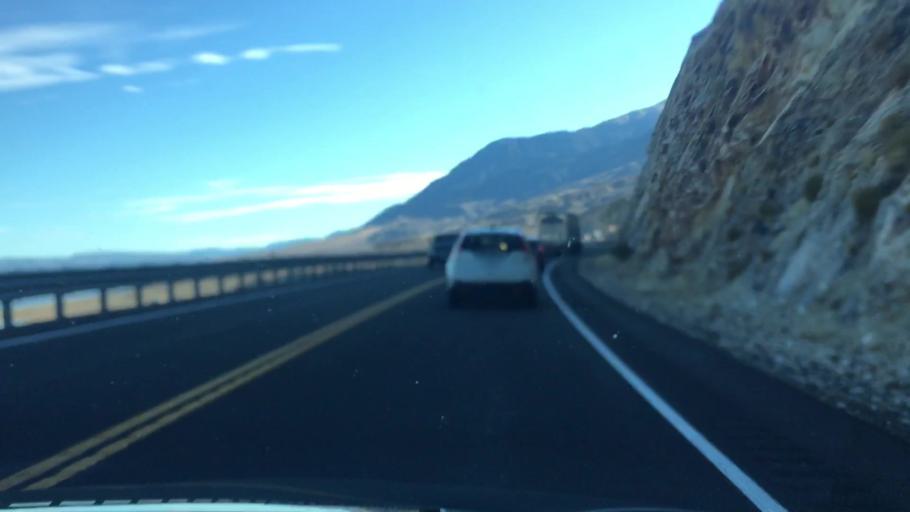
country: US
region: Nevada
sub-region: Mineral County
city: Hawthorne
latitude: 38.6686
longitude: -118.7679
